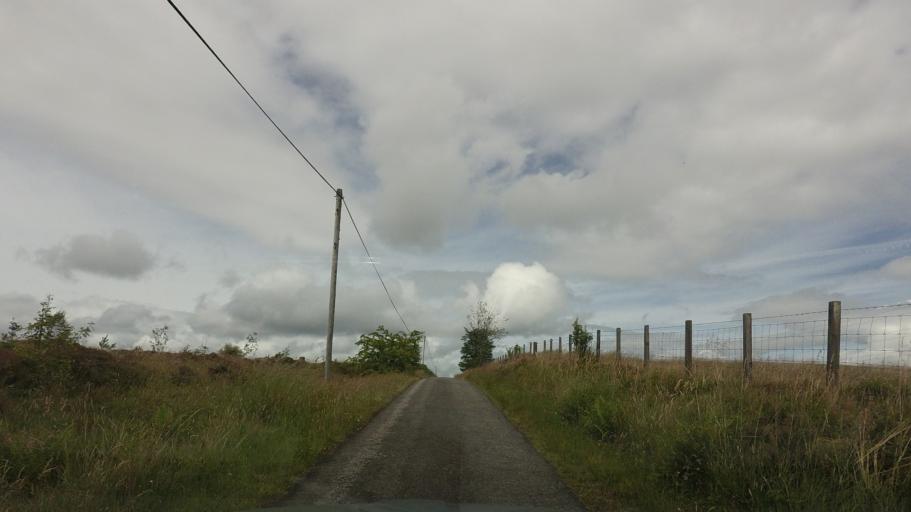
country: GB
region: Scotland
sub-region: Stirling
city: Killearn
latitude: 56.0937
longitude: -4.4319
